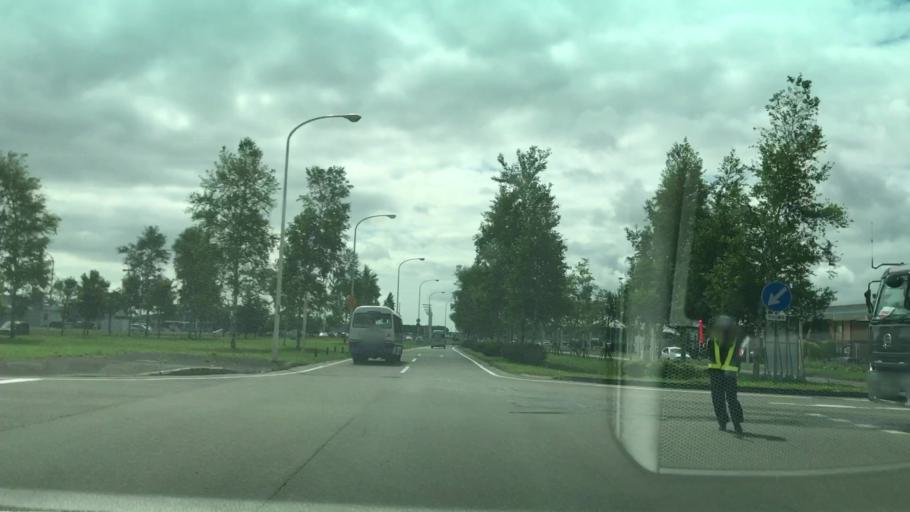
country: JP
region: Hokkaido
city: Chitose
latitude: 42.7834
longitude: 141.6775
